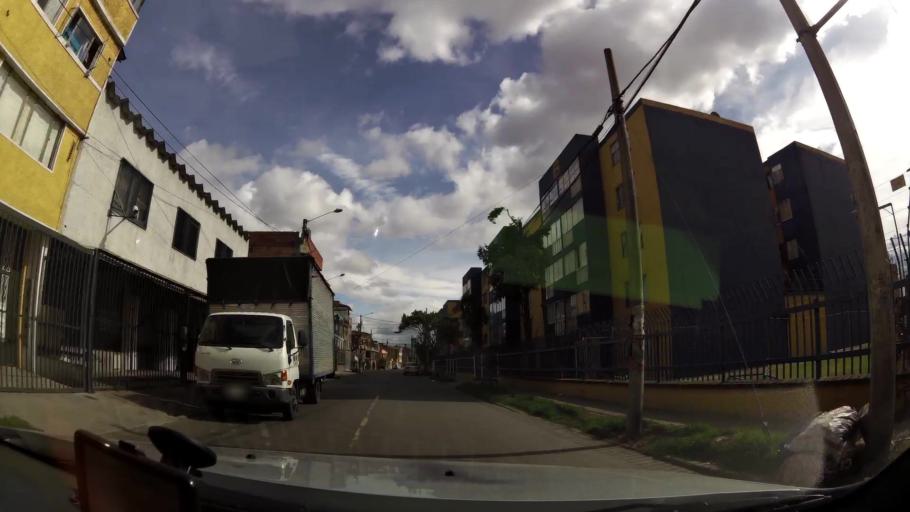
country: CO
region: Bogota D.C.
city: Bogota
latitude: 4.6089
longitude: -74.1407
